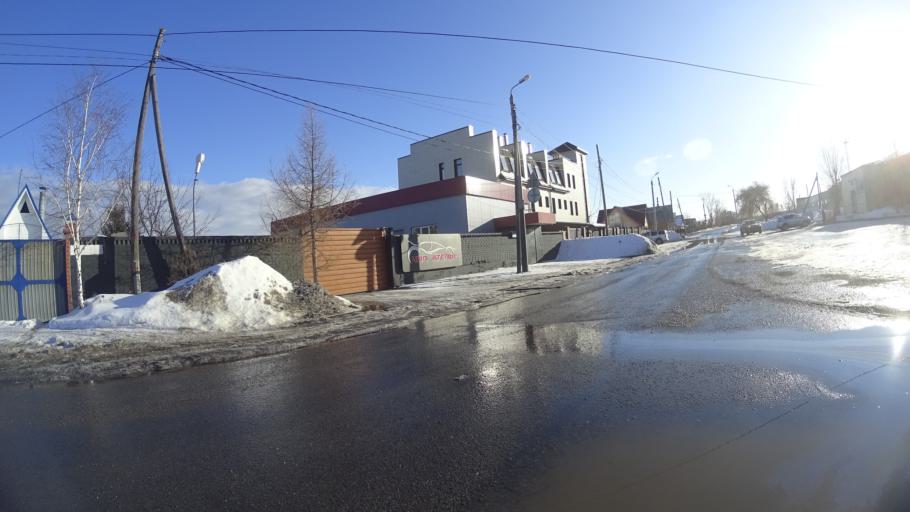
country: RU
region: Chelyabinsk
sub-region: Gorod Chelyabinsk
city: Chelyabinsk
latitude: 55.1505
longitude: 61.3081
